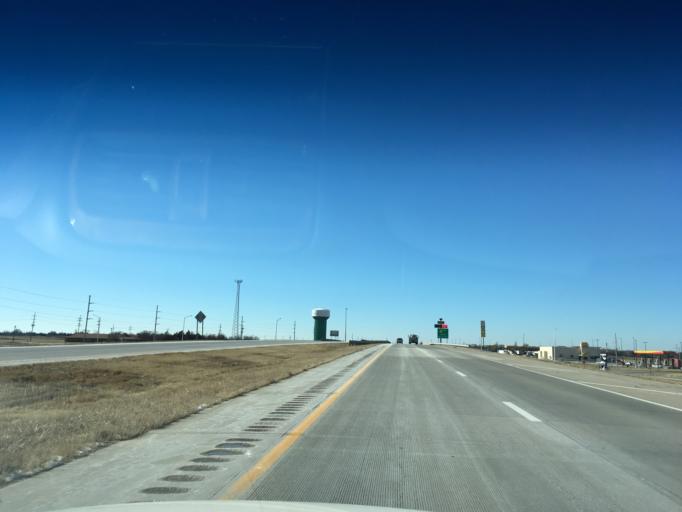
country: US
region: Kansas
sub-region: Reno County
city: South Hutchinson
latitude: 38.0133
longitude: -97.9374
